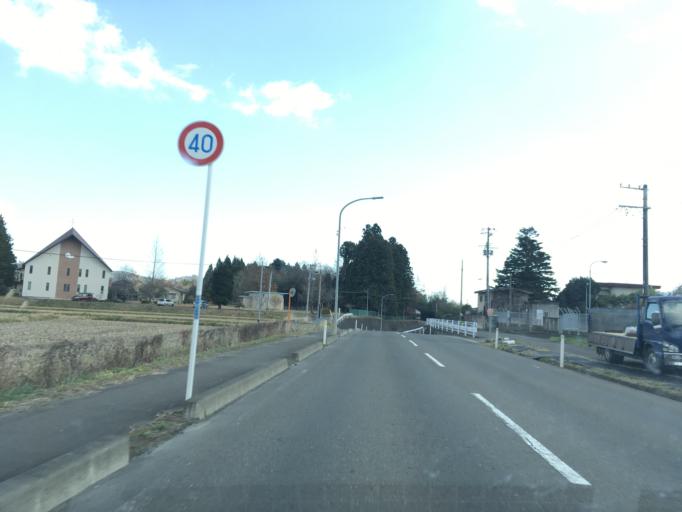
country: JP
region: Miyagi
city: Sendai
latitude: 38.2810
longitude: 140.7576
